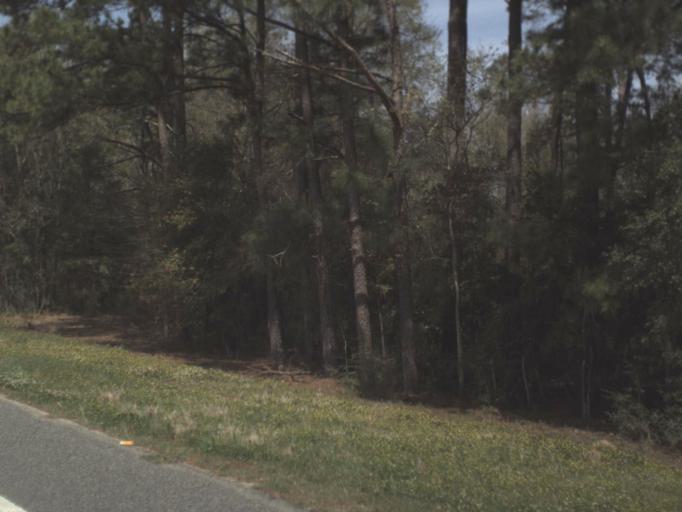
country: US
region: Florida
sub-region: Walton County
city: DeFuniak Springs
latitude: 30.7271
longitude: -85.9682
